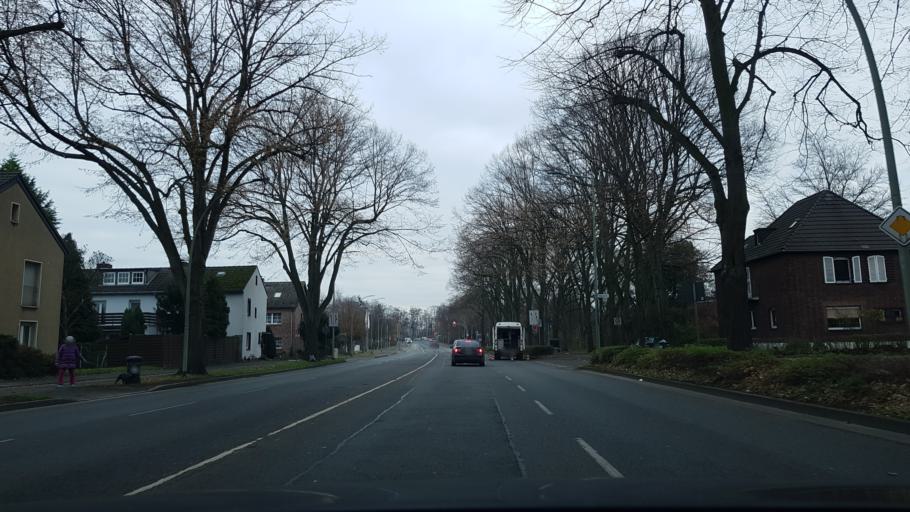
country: DE
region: North Rhine-Westphalia
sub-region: Regierungsbezirk Dusseldorf
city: Hochfeld
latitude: 51.4548
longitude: 6.7053
